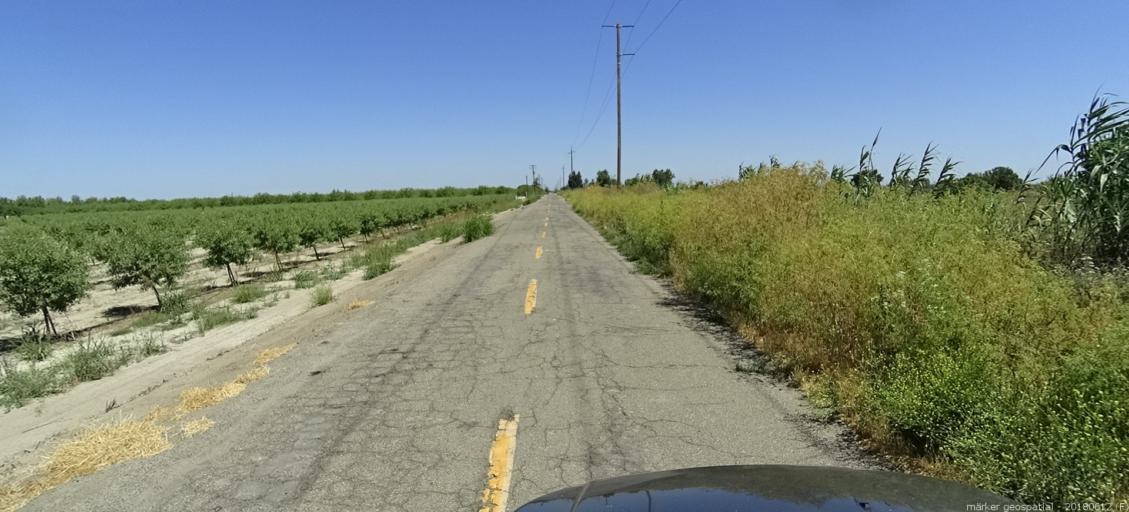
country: US
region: California
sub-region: Madera County
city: Chowchilla
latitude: 37.0130
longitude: -120.3286
